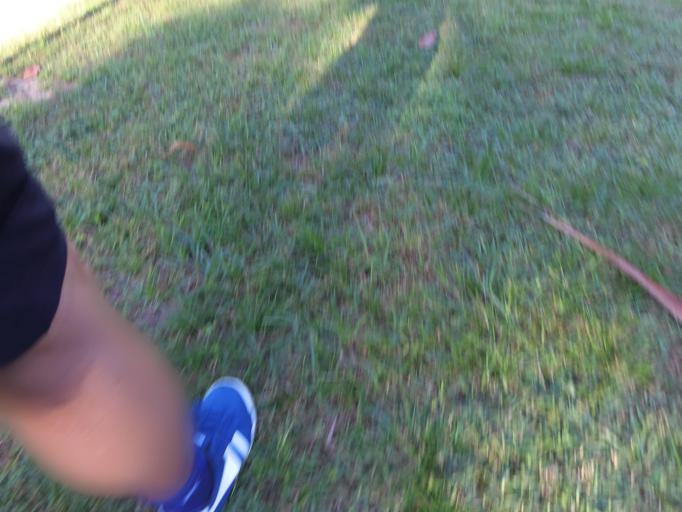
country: US
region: Florida
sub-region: Marion County
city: Citra
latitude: 29.4810
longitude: -82.1602
